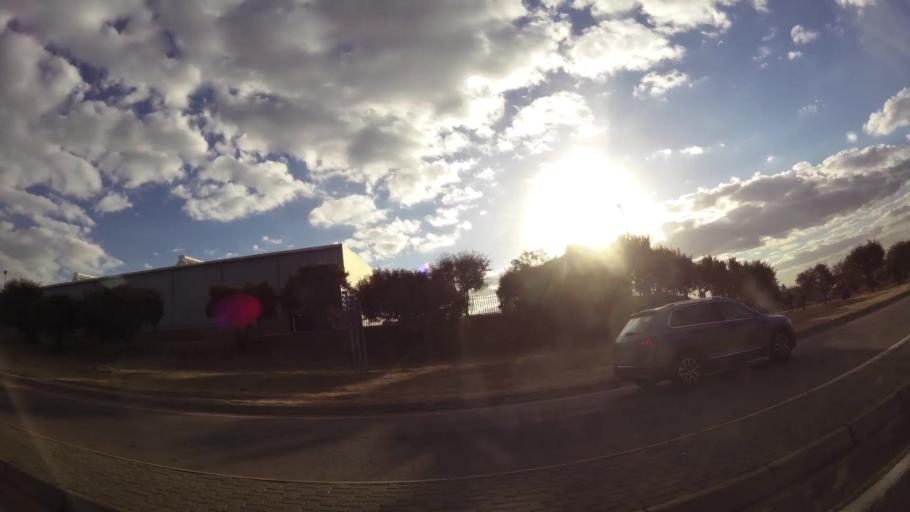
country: ZA
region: Gauteng
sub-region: City of Tshwane Metropolitan Municipality
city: Centurion
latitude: -25.9121
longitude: 28.1646
